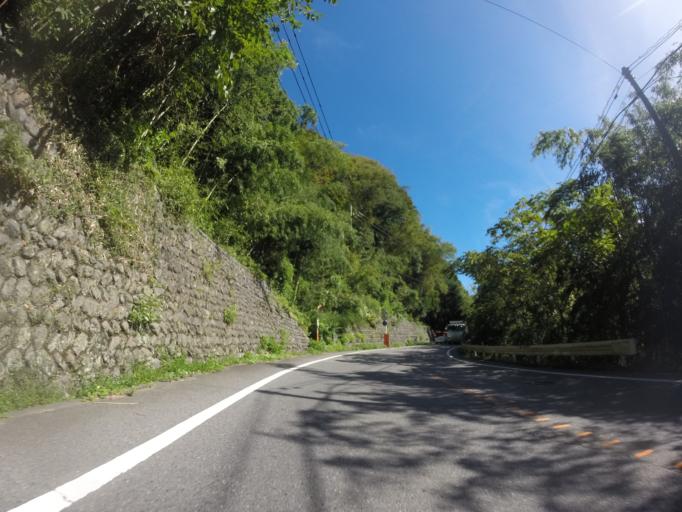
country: JP
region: Shizuoka
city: Fujinomiya
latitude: 35.3477
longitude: 138.4507
